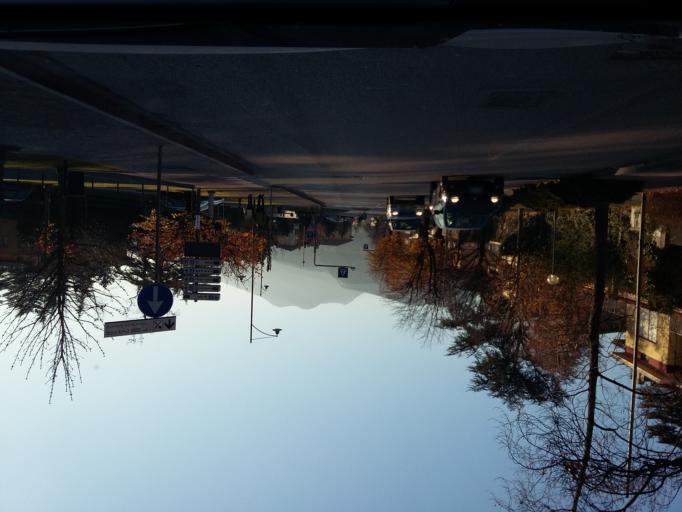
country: IT
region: Trentino-Alto Adige
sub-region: Provincia di Trento
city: Rovereto
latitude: 45.8995
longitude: 11.0422
